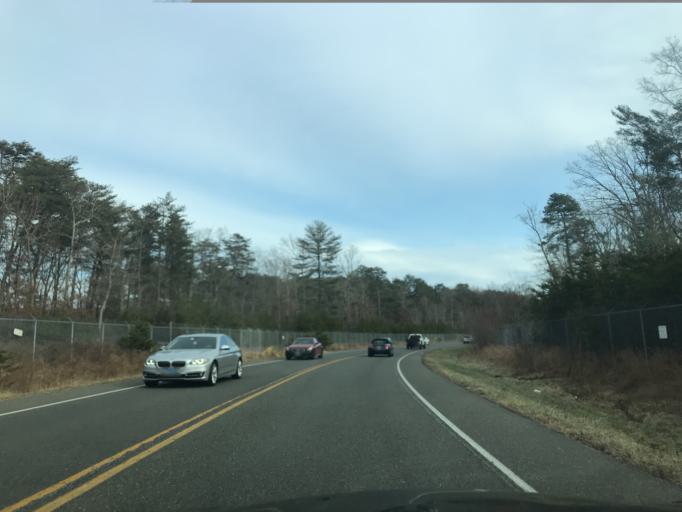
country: US
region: Maryland
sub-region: Prince George's County
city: Goddard
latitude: 39.0034
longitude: -76.8378
